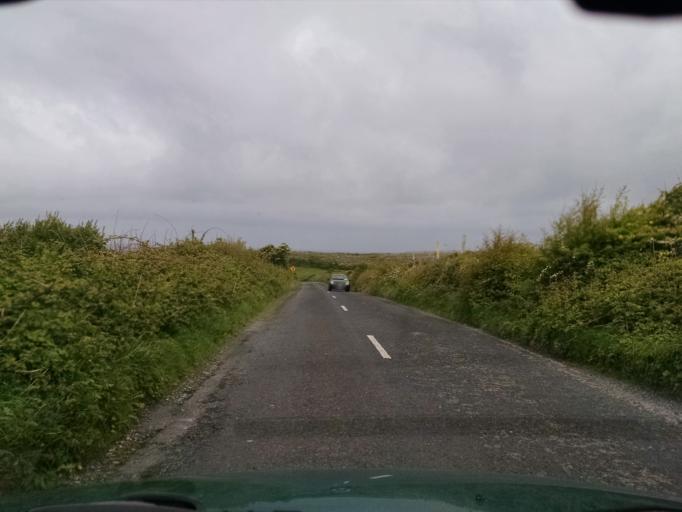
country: IE
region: Connaught
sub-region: County Galway
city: Bearna
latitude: 53.0535
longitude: -9.3482
